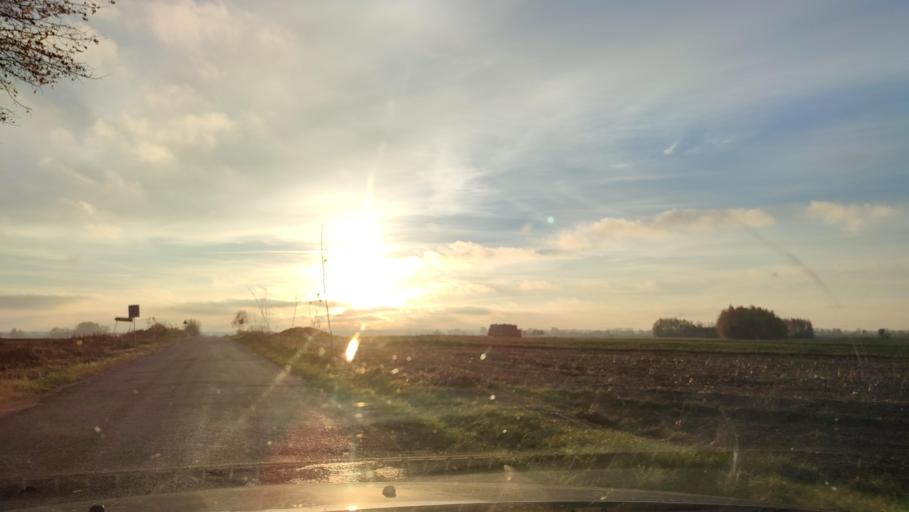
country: PL
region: Masovian Voivodeship
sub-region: Powiat mlawski
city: Wieczfnia Koscielna
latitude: 53.2408
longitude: 20.5774
